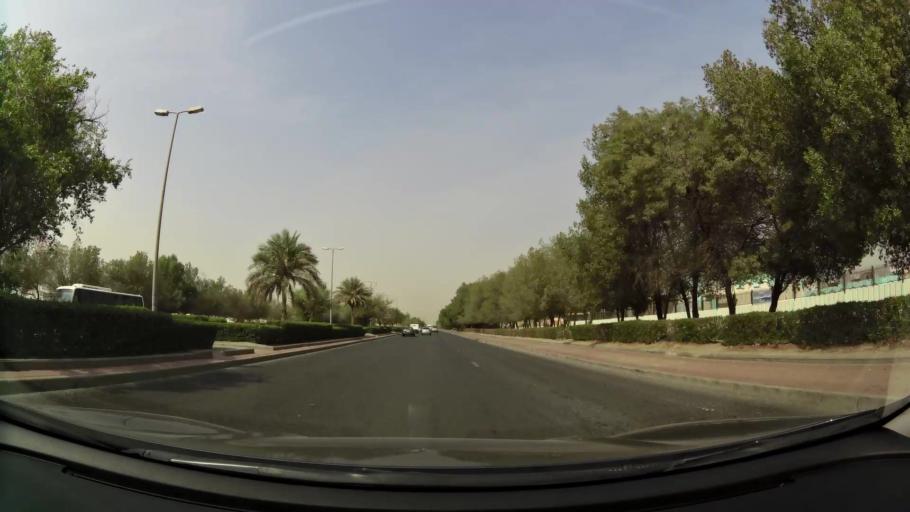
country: KW
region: Al Asimah
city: Ar Rabiyah
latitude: 29.2571
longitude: 47.9173
